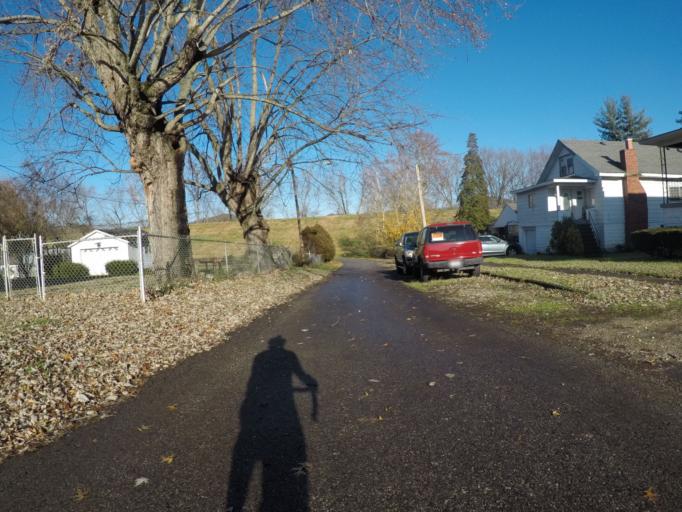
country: US
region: Ohio
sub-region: Lawrence County
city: Burlington
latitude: 38.4090
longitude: -82.4966
